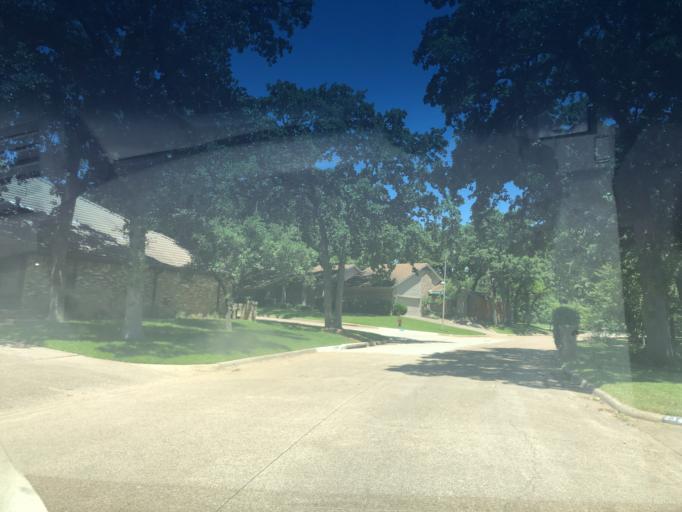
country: US
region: Texas
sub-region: Dallas County
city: Grand Prairie
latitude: 32.7791
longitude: -97.0388
